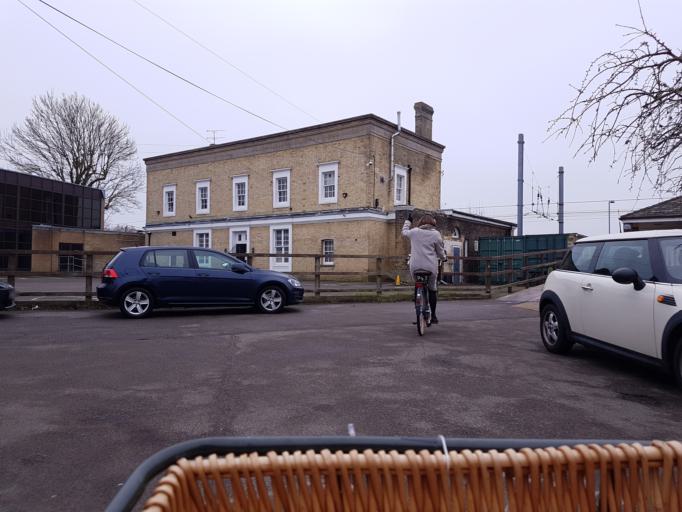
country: GB
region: England
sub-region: Cambridgeshire
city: Duxford
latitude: 52.0603
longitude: 0.1936
